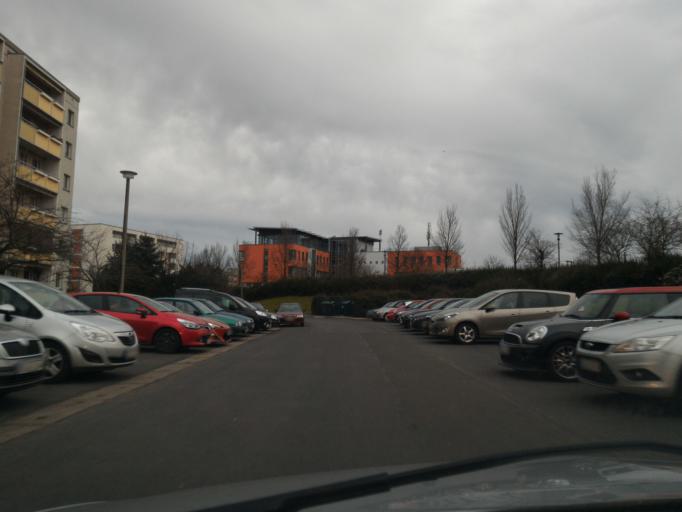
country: DE
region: Saxony
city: Bannewitz
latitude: 51.0202
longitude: 13.7166
